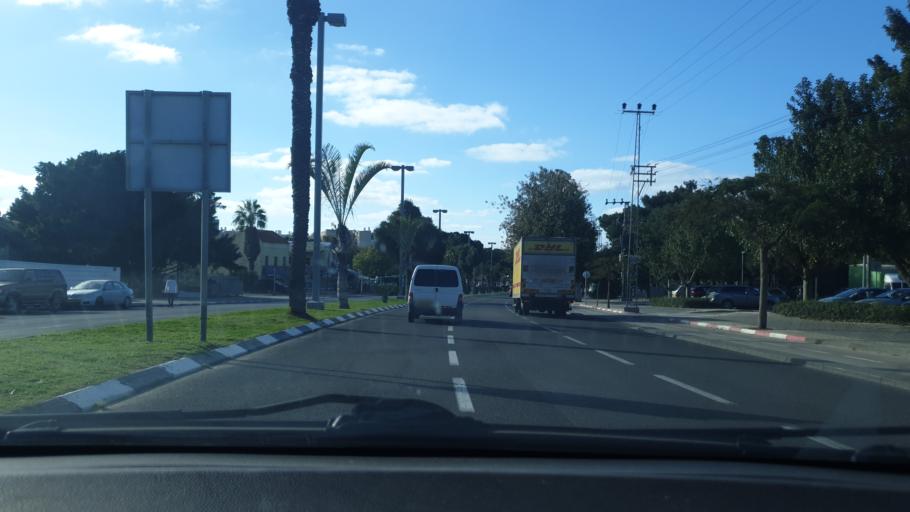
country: IL
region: Tel Aviv
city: Yafo
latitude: 32.0435
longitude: 34.7700
